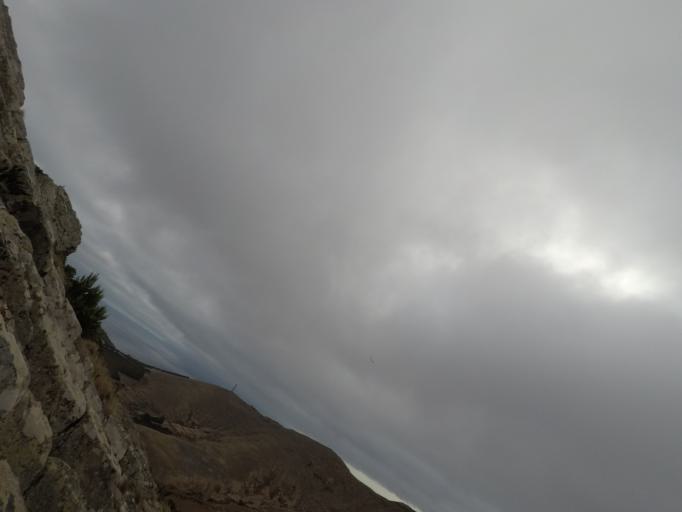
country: PT
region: Madeira
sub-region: Porto Santo
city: Vila de Porto Santo
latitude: 33.0455
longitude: -16.3691
